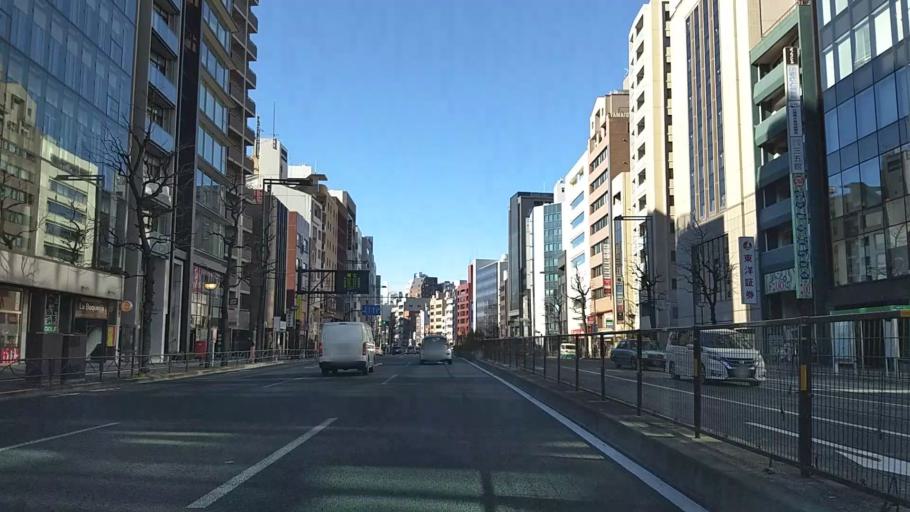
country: JP
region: Tokyo
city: Tokyo
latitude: 35.6874
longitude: 139.7250
